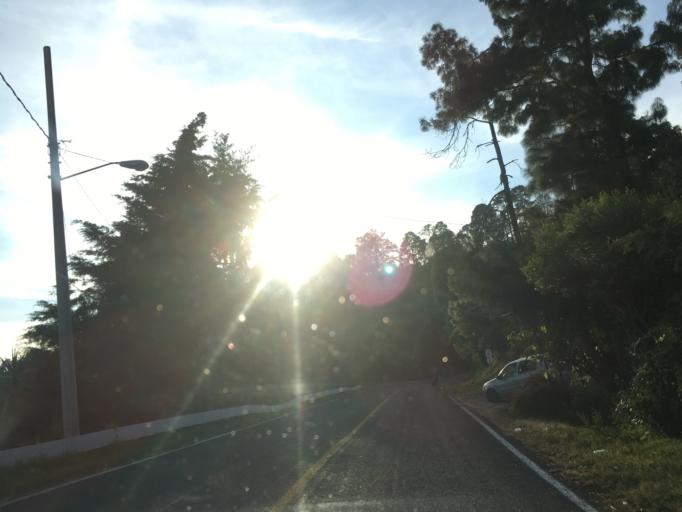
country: MX
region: Michoacan
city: Tzitzio
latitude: 19.6742
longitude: -100.9055
